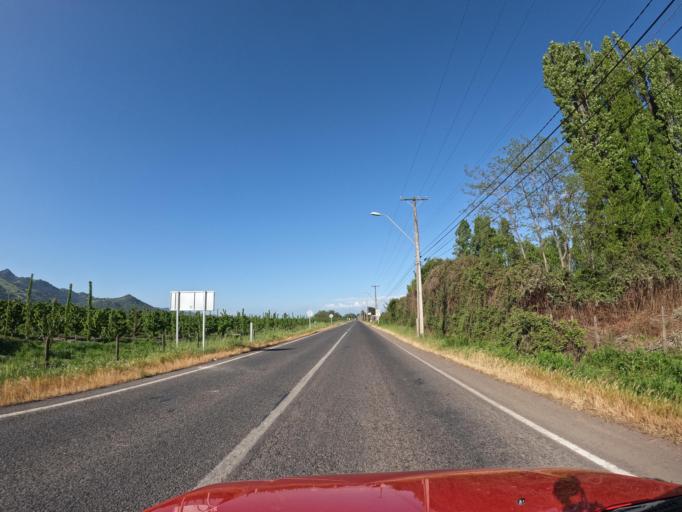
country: CL
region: Maule
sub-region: Provincia de Curico
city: Teno
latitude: -34.8724
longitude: -71.2244
